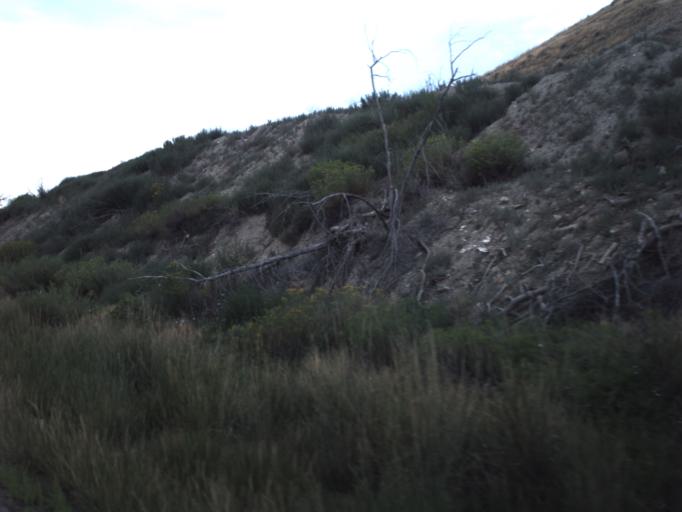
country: US
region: Utah
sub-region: Emery County
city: Huntington
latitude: 39.3684
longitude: -110.8506
